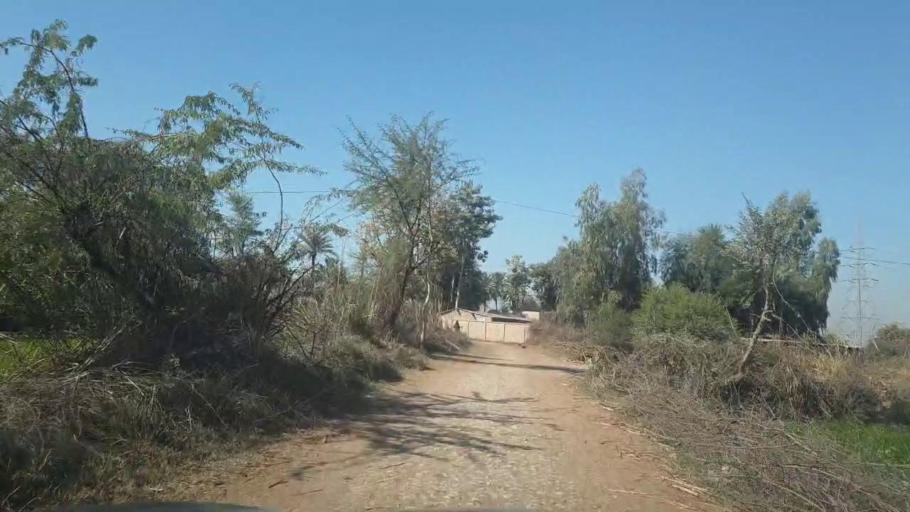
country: PK
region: Sindh
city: Adilpur
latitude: 27.8956
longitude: 69.2764
